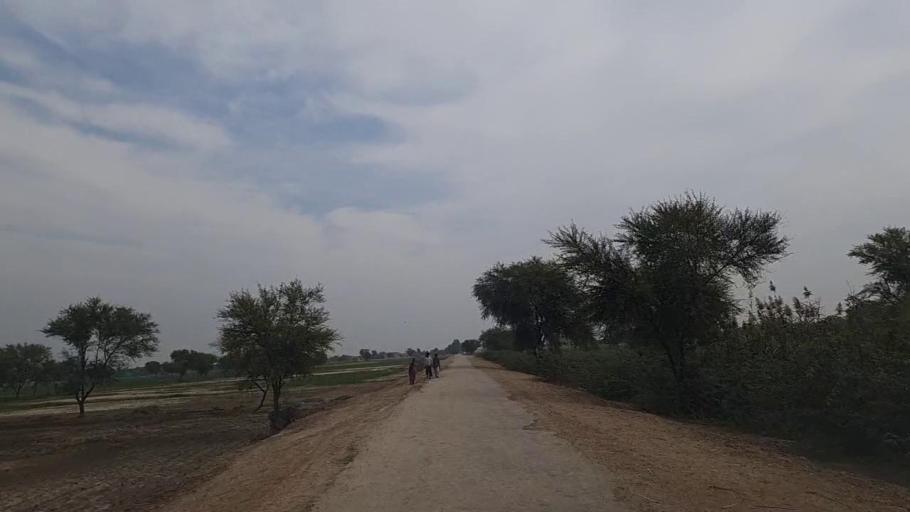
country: PK
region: Sindh
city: Daur
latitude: 26.4449
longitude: 68.4724
